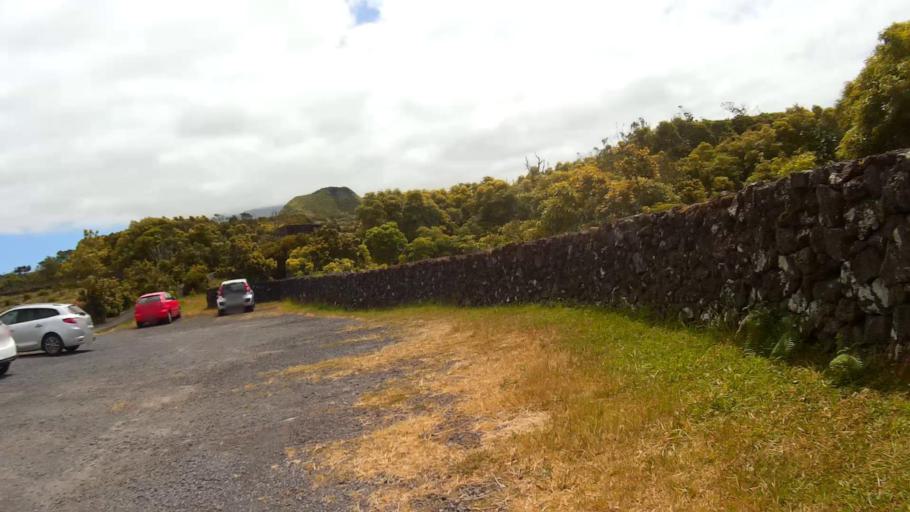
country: PT
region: Azores
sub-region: Madalena
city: Madalena
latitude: 38.4946
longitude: -28.5035
